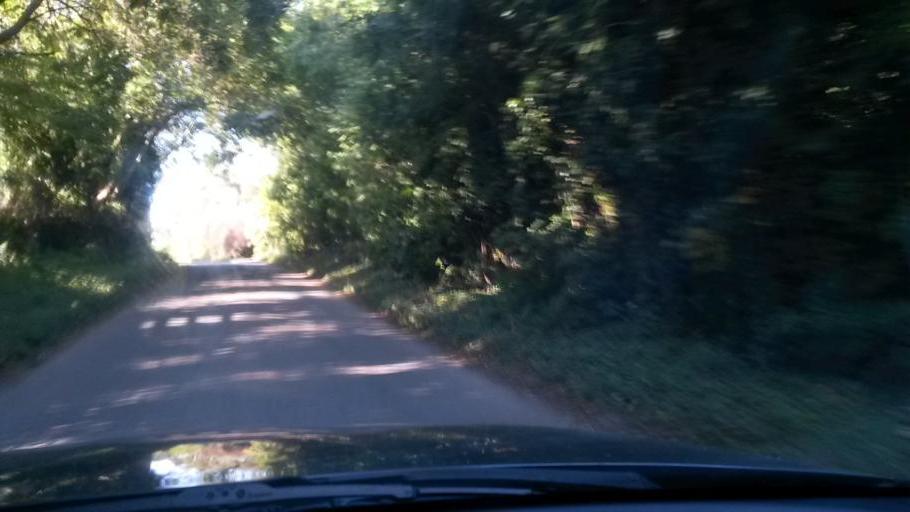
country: IE
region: Leinster
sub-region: Fingal County
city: Swords
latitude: 53.4920
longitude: -6.2846
